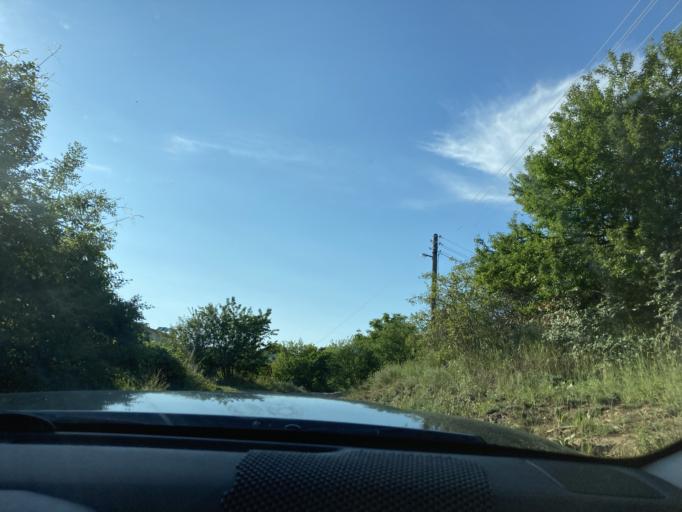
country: BG
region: Sofiya
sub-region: Obshtina Slivnitsa
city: Slivnitsa
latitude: 42.8501
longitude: 22.9900
